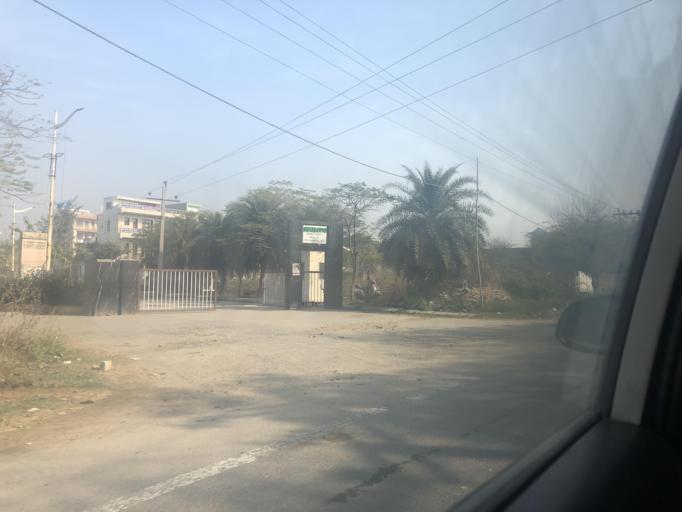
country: IN
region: Haryana
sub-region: Jhajjar
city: Bahadurgarh
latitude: 28.6867
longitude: 76.8952
